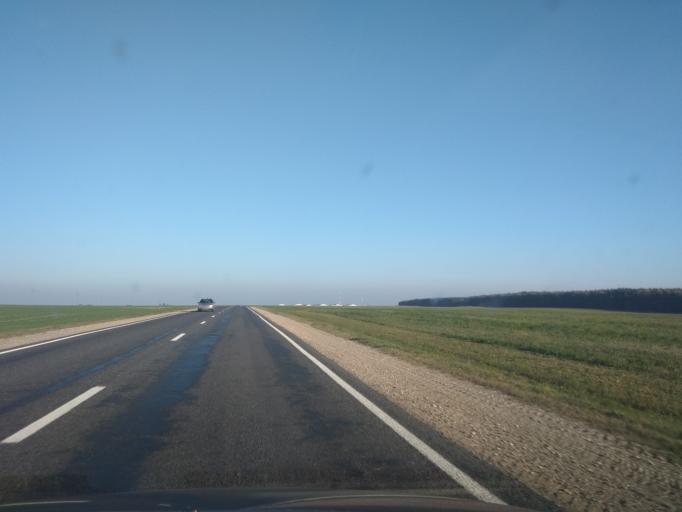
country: BY
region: Grodnenskaya
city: Svislach
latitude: 53.1292
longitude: 24.1513
